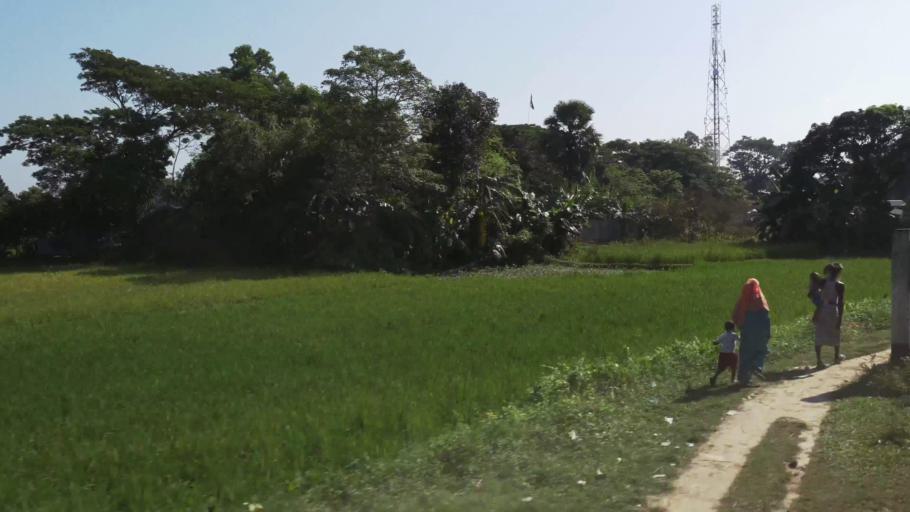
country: BD
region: Dhaka
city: Gafargaon
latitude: 24.5296
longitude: 90.5086
